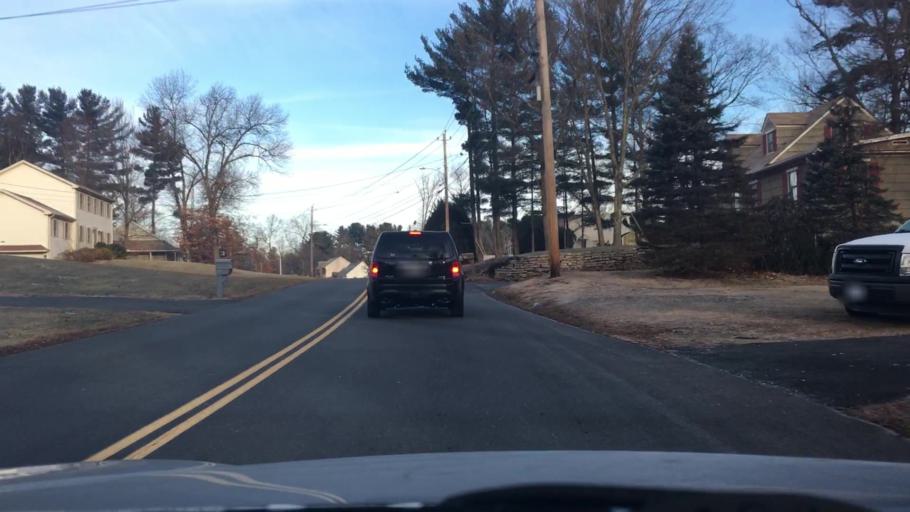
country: US
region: Massachusetts
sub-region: Hampden County
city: Westfield
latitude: 42.1324
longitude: -72.7228
